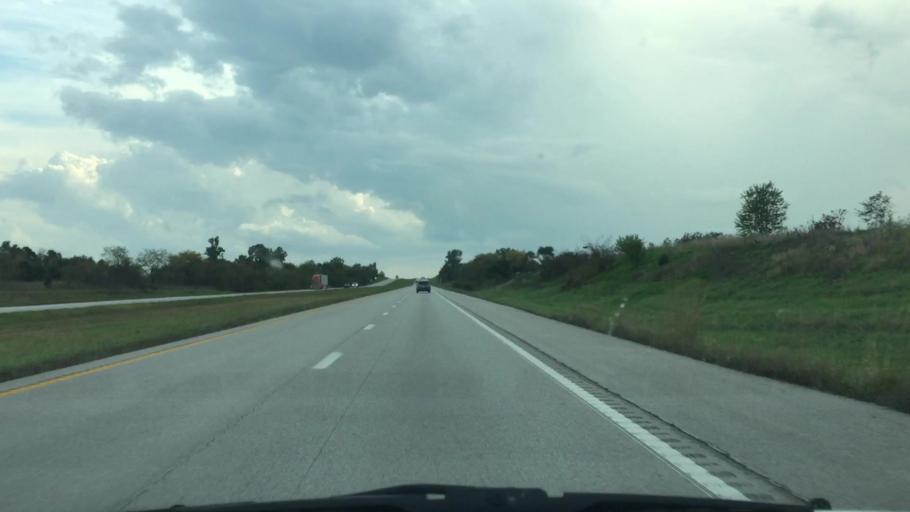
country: US
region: Missouri
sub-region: Clinton County
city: Cameron
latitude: 39.8193
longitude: -94.1923
